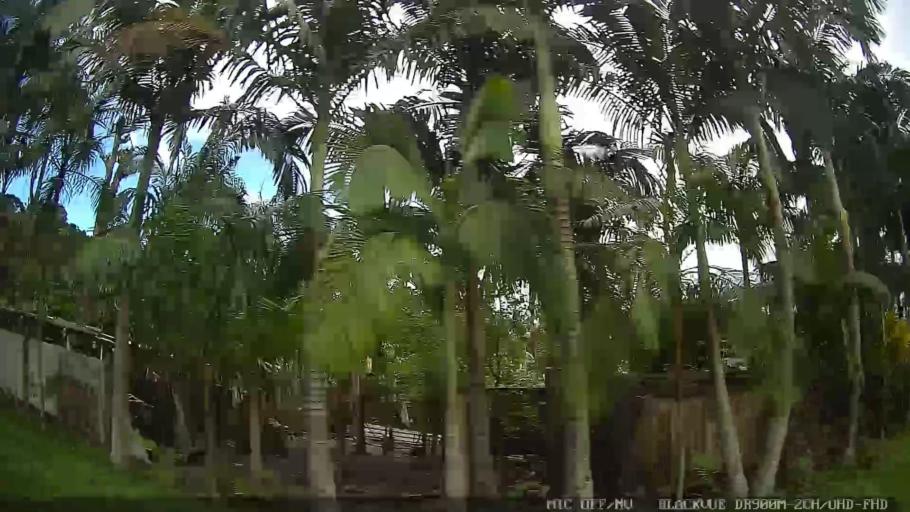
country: BR
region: Sao Paulo
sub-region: Iguape
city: Iguape
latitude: -24.6627
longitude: -47.4215
